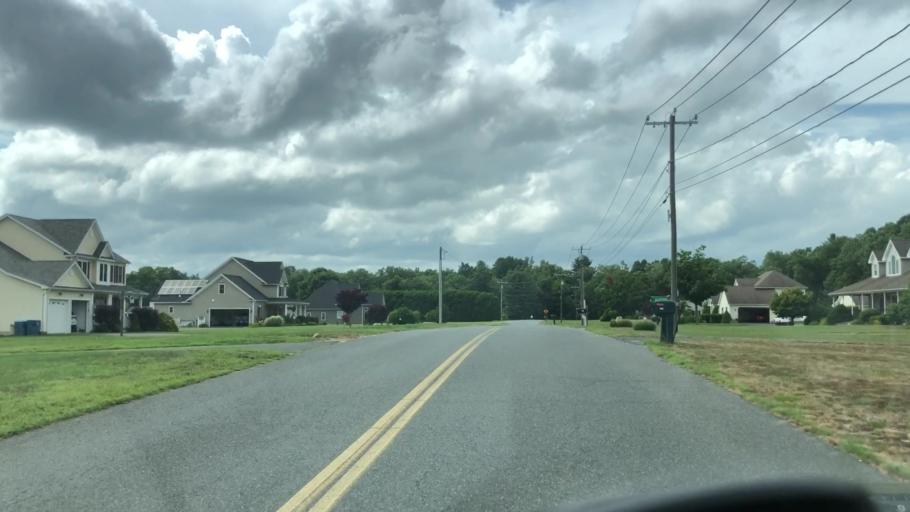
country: US
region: Massachusetts
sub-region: Hampshire County
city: Easthampton
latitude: 42.2368
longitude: -72.6886
